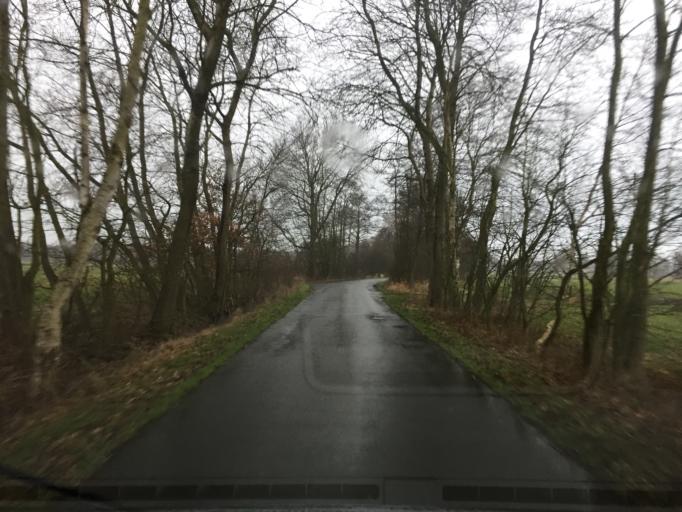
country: DE
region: Lower Saxony
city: Maasen
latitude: 52.6487
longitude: 8.8801
